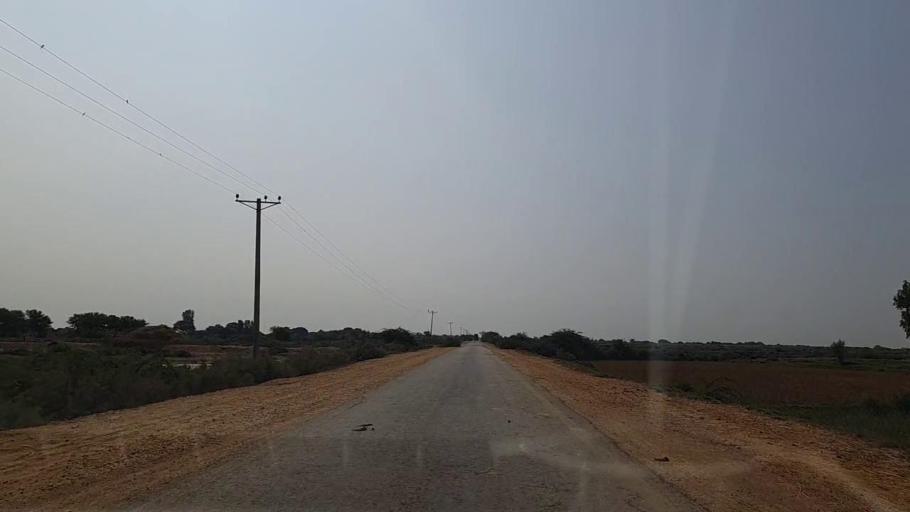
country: PK
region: Sindh
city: Chuhar Jamali
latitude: 24.2821
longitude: 67.9204
